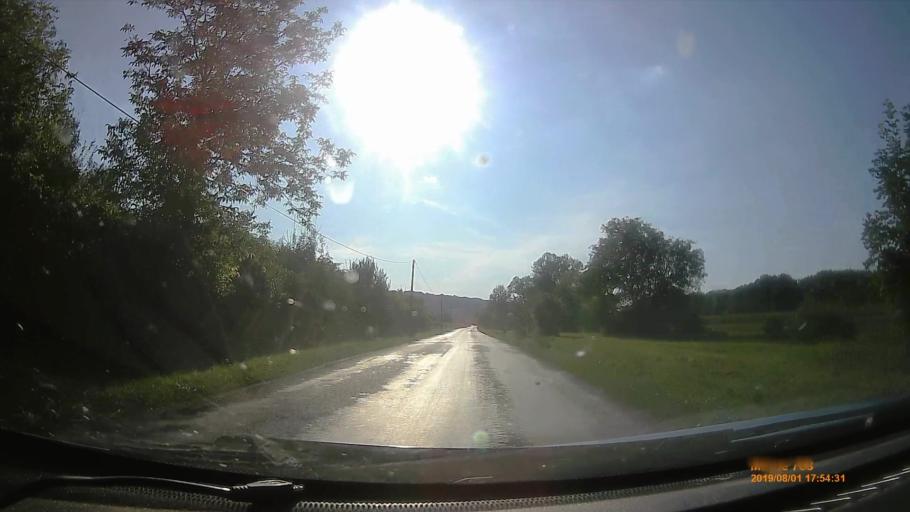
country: HU
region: Baranya
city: Sasd
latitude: 46.1924
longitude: 18.1495
